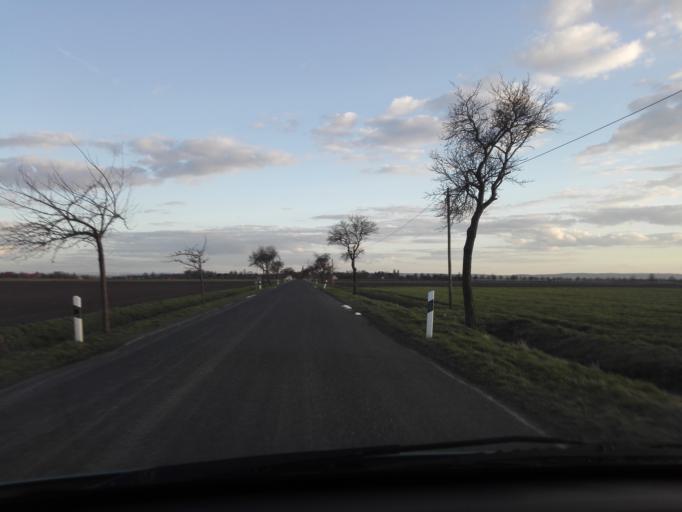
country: DE
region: Lower Saxony
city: Hohenhameln
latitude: 52.2553
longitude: 10.1137
